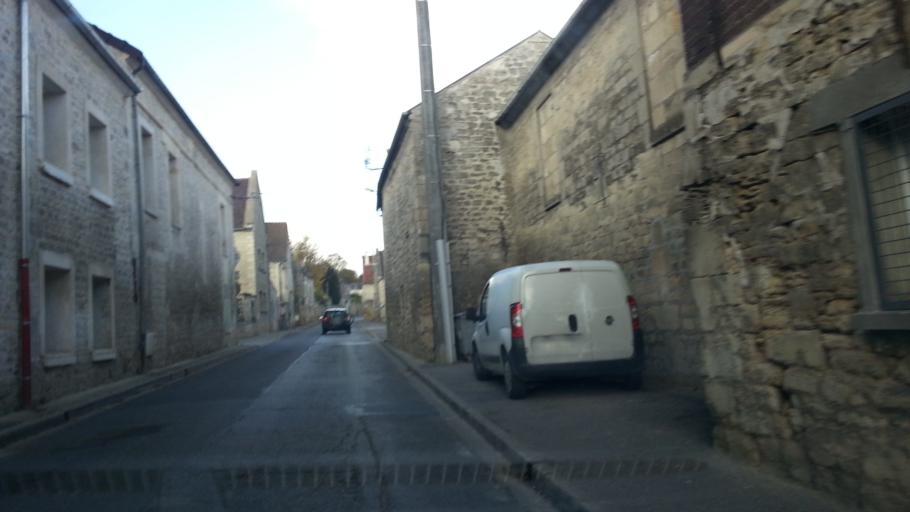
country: FR
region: Picardie
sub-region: Departement de l'Oise
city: Villers-sous-Saint-Leu
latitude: 49.2172
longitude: 2.4170
